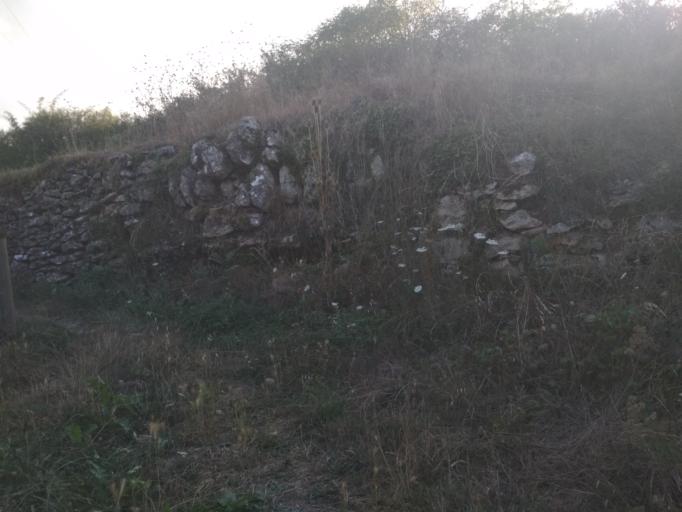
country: ES
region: Catalonia
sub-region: Provincia de Barcelona
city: Castelltercol
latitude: 41.7593
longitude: 2.1238
